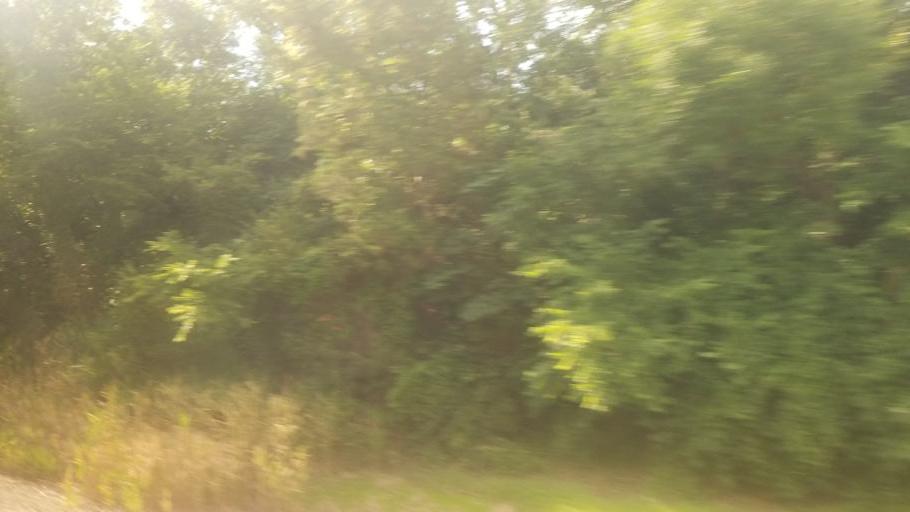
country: US
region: Kansas
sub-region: Johnson County
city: De Soto
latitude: 38.9814
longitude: -94.9718
